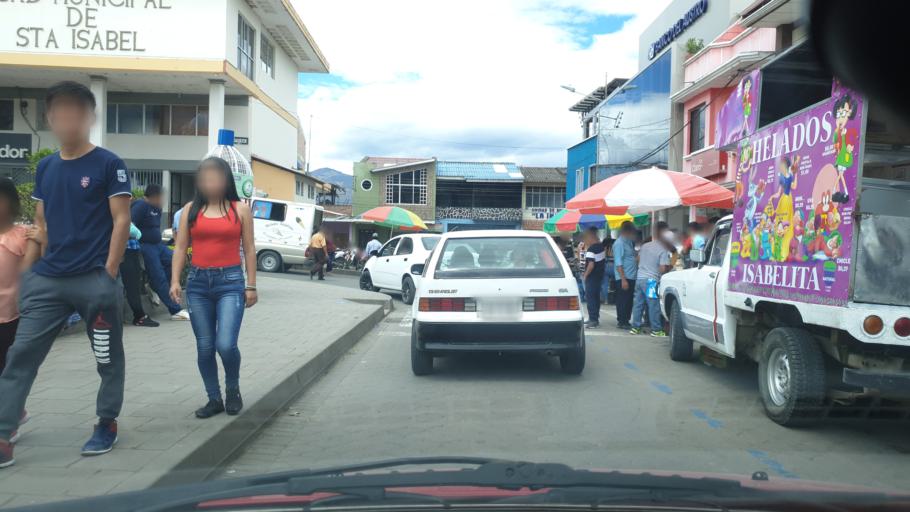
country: EC
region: Azuay
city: Cuenca
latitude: -3.2743
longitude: -79.3154
